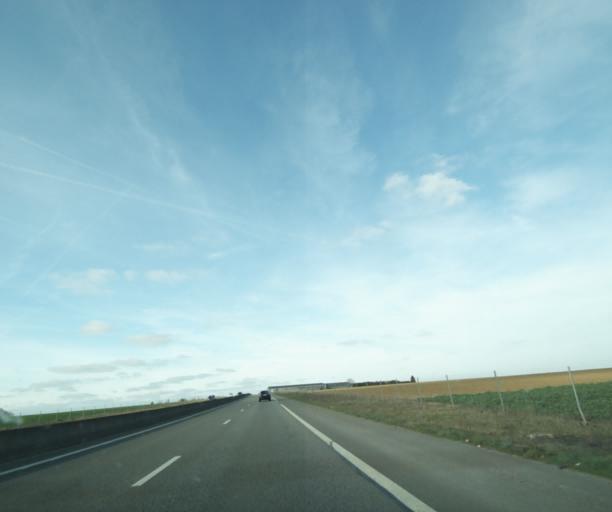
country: FR
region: Ile-de-France
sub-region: Departement des Yvelines
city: Ablis
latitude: 48.5591
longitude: 1.8317
